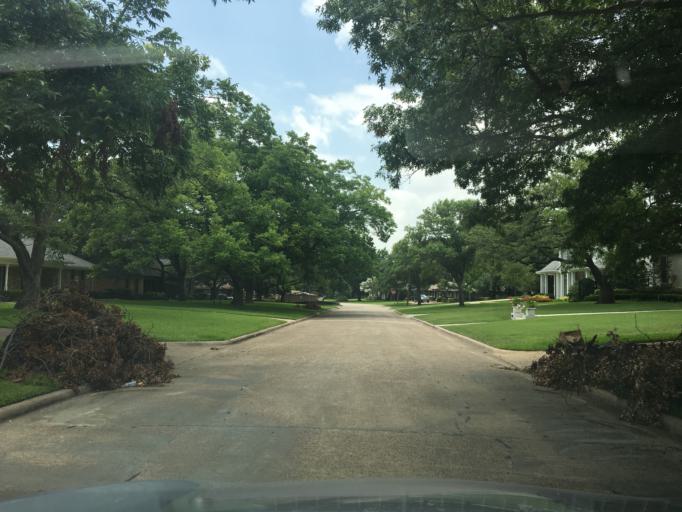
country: US
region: Texas
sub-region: Dallas County
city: University Park
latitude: 32.8975
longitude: -96.8323
